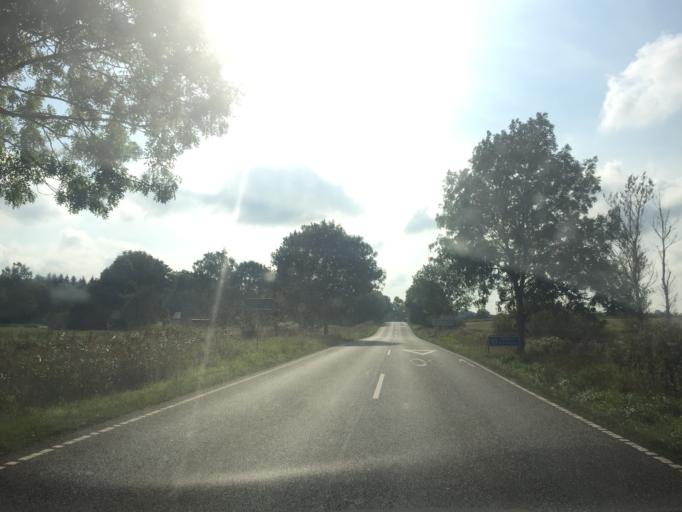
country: DK
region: Zealand
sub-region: Holbaek Kommune
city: Tollose
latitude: 55.6358
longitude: 11.7979
